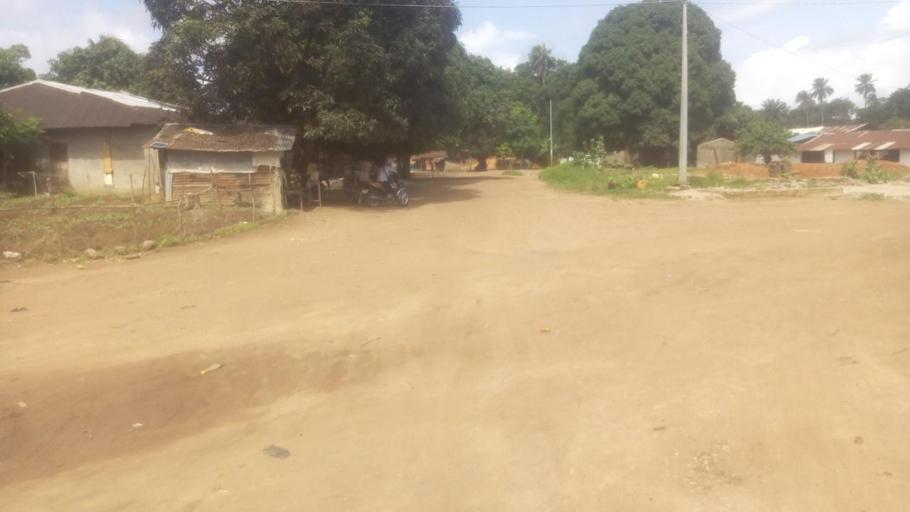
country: SL
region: Northern Province
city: Tintafor
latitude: 8.6395
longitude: -13.2257
